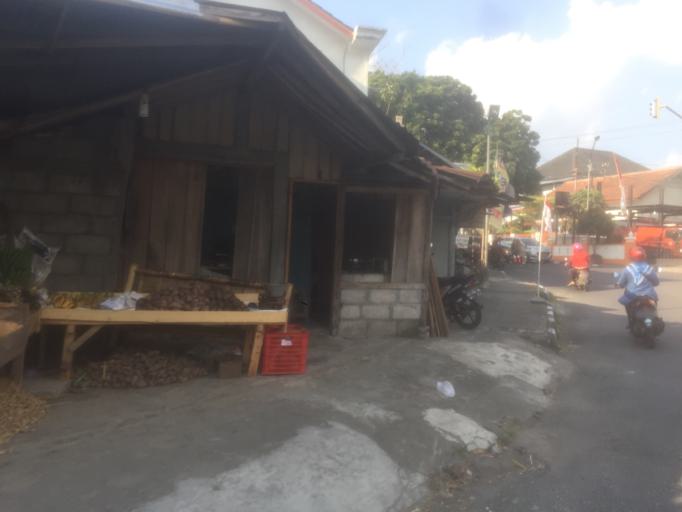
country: ID
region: Daerah Istimewa Yogyakarta
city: Sleman
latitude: -7.6673
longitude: 110.4186
